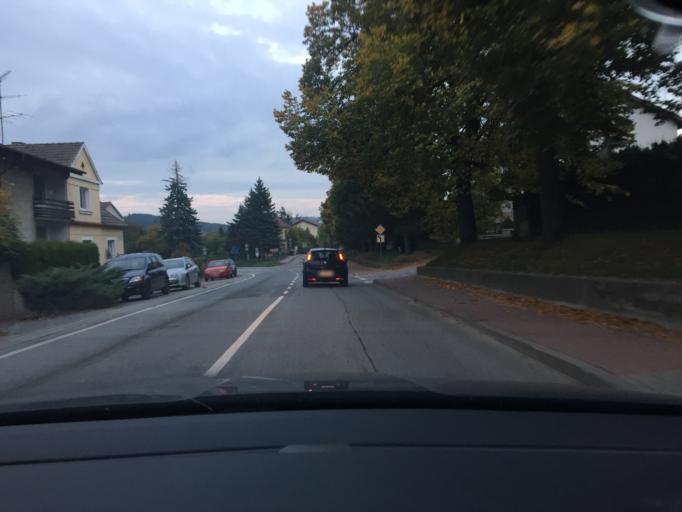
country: CZ
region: Jihocesky
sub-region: Okres Ceske Budejovice
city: Hluboka nad Vltavou
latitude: 49.0548
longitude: 14.4538
